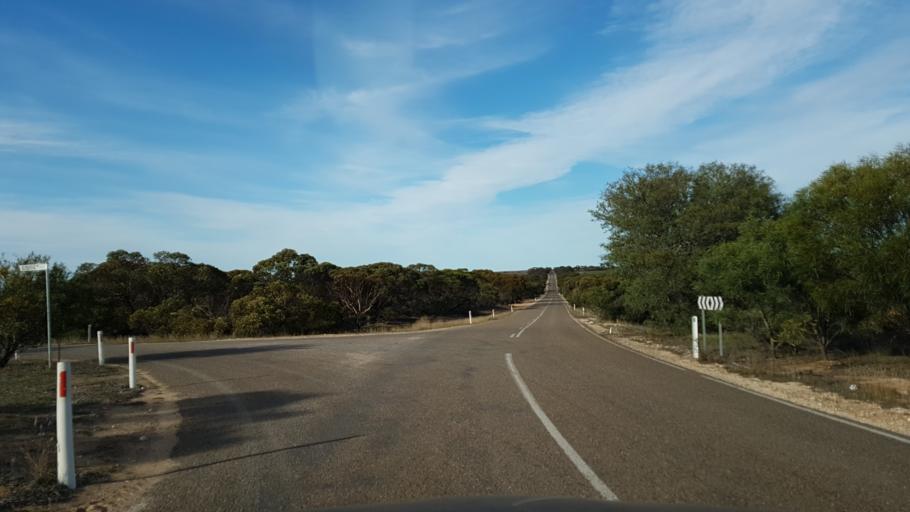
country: AU
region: South Australia
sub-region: Murray Bridge
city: Murray Bridge
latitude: -35.0440
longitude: 139.4654
